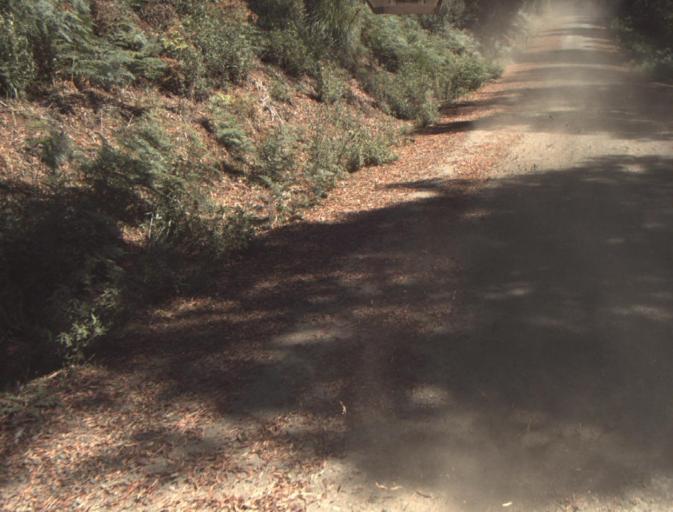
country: AU
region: Tasmania
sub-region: Dorset
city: Scottsdale
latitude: -41.3784
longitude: 147.4855
